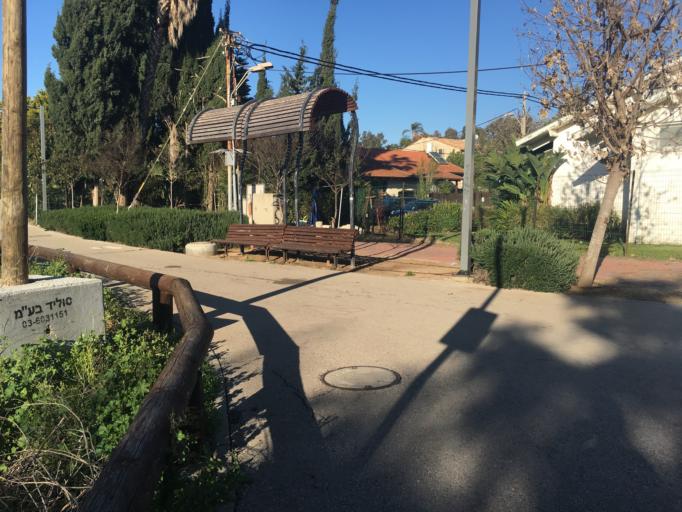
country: IL
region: Tel Aviv
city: Ramat HaSharon
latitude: 32.1418
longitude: 34.8256
